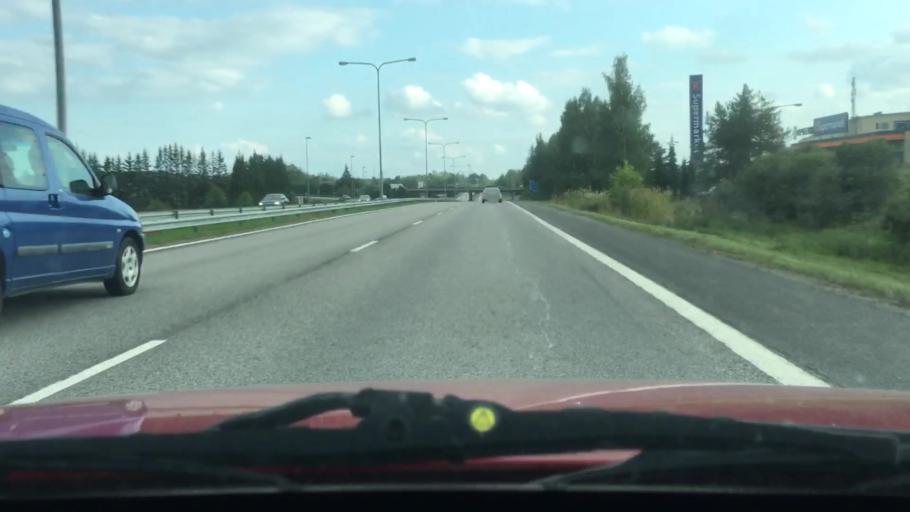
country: FI
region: Varsinais-Suomi
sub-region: Turku
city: Raisio
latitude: 60.4913
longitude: 22.1705
